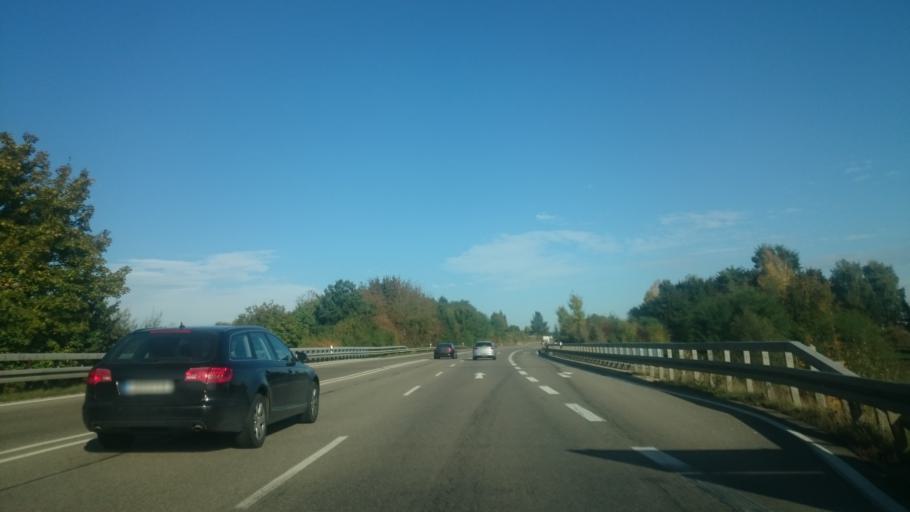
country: DE
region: Bavaria
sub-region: Regierungsbezirk Mittelfranken
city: Ellingen
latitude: 49.0603
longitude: 10.9588
